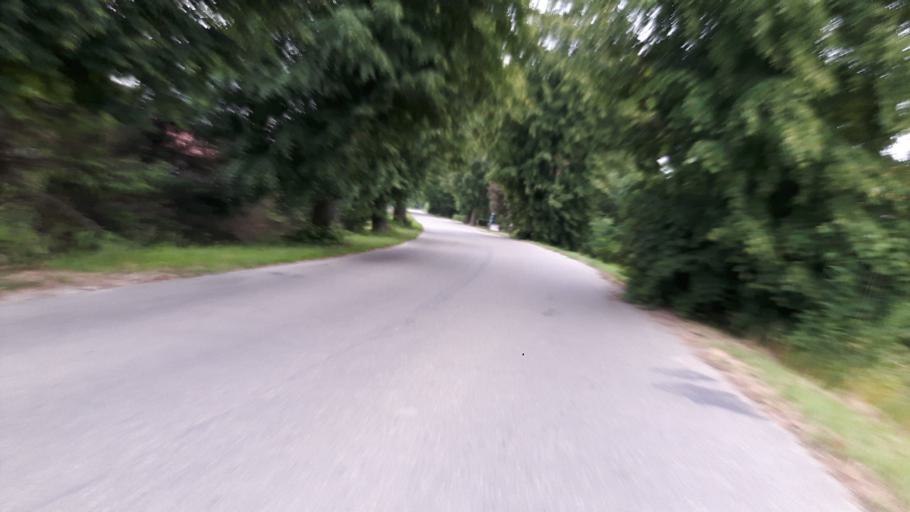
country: PL
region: Warmian-Masurian Voivodeship
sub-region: Powiat elblaski
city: Elblag
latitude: 54.2147
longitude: 19.3698
